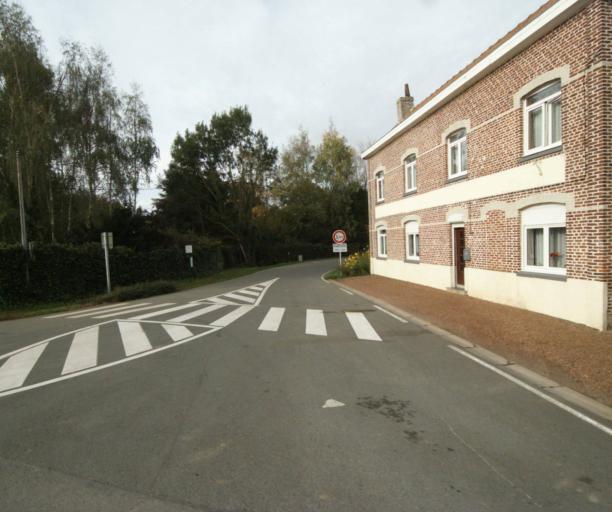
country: FR
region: Nord-Pas-de-Calais
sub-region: Departement du Nord
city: Aubers
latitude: 50.6124
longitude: 2.8486
